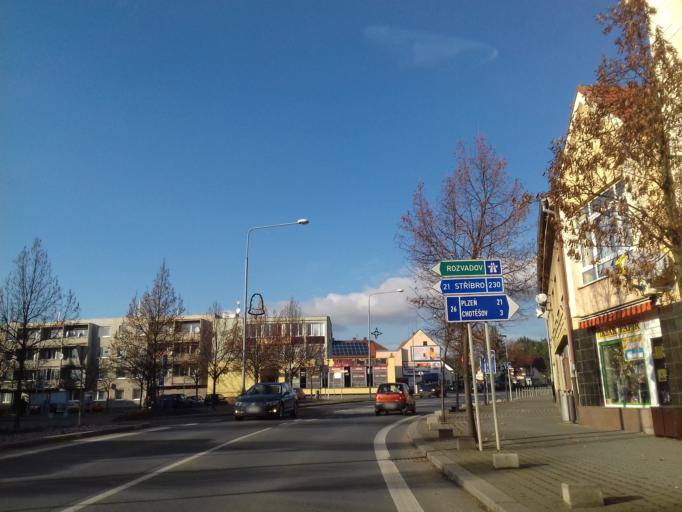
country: CZ
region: Plzensky
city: Stod
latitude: 49.6395
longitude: 13.1646
